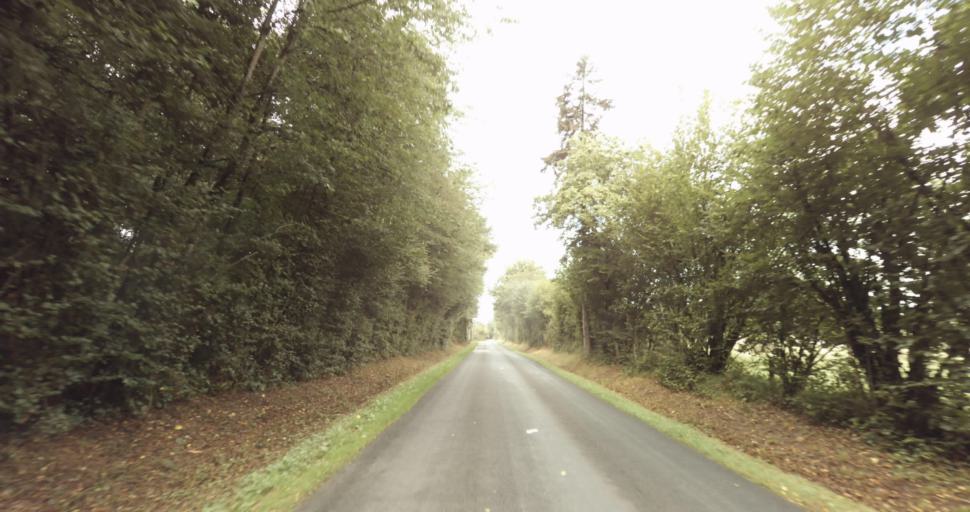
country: FR
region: Lower Normandy
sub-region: Departement de l'Orne
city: Gace
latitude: 48.8022
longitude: 0.2553
